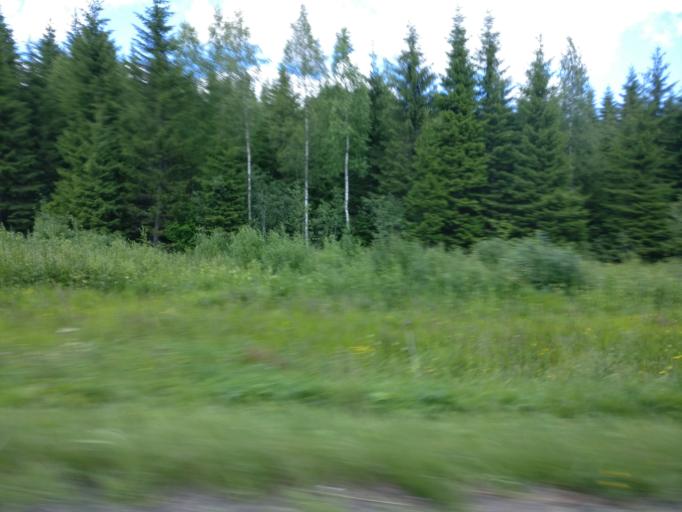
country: FI
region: Southern Savonia
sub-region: Savonlinna
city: Kerimaeki
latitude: 61.8594
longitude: 29.1549
